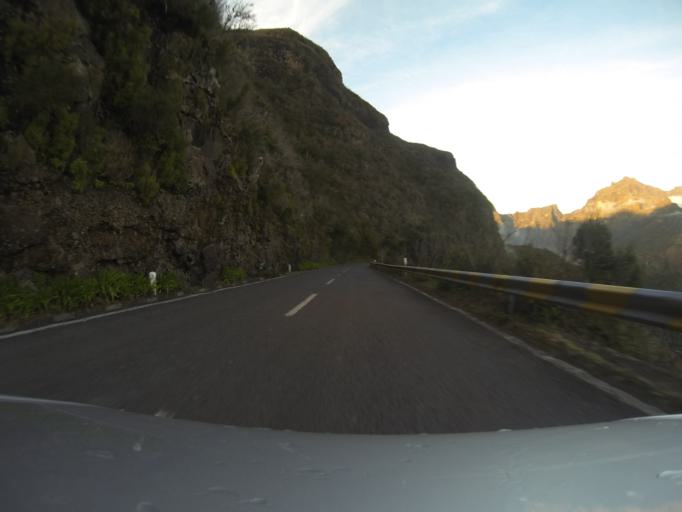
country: PT
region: Madeira
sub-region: Sao Vicente
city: Sao Vicente
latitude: 32.7529
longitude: -17.0276
